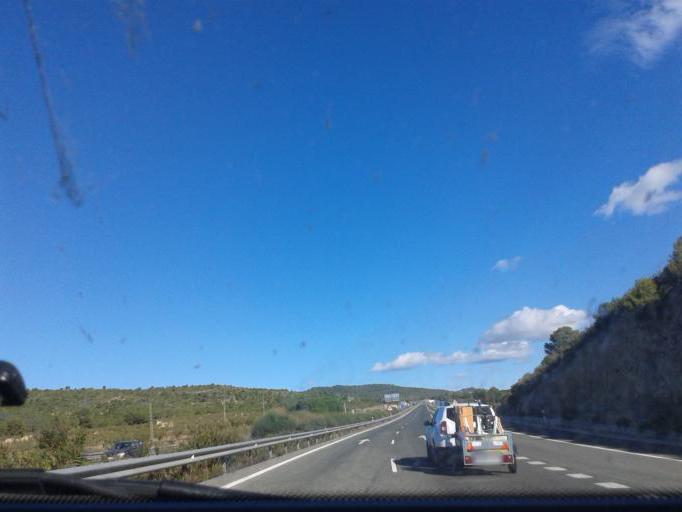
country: ES
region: Valencia
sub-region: Provincia de Alicante
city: Biar
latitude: 38.5799
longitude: -0.7808
